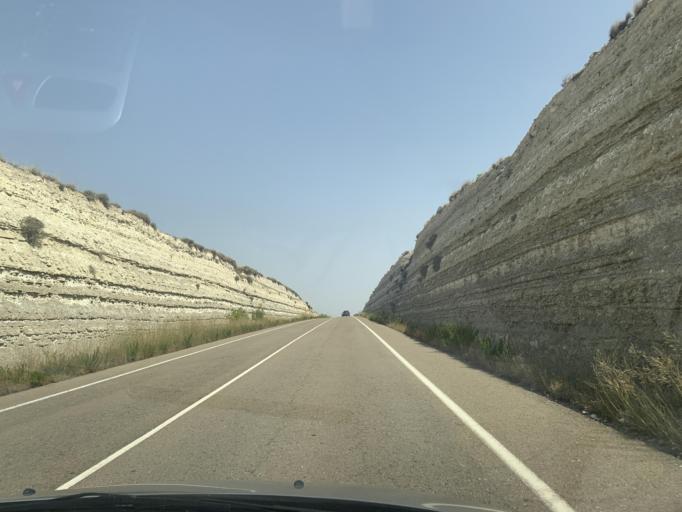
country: ES
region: Aragon
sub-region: Provincia de Zaragoza
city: Belchite
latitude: 41.4243
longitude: -0.7264
